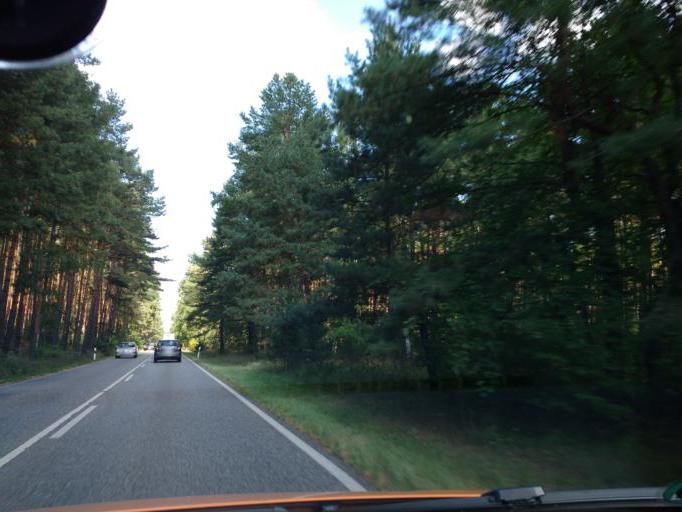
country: DE
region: Brandenburg
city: Oranienburg
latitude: 52.7265
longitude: 13.2668
